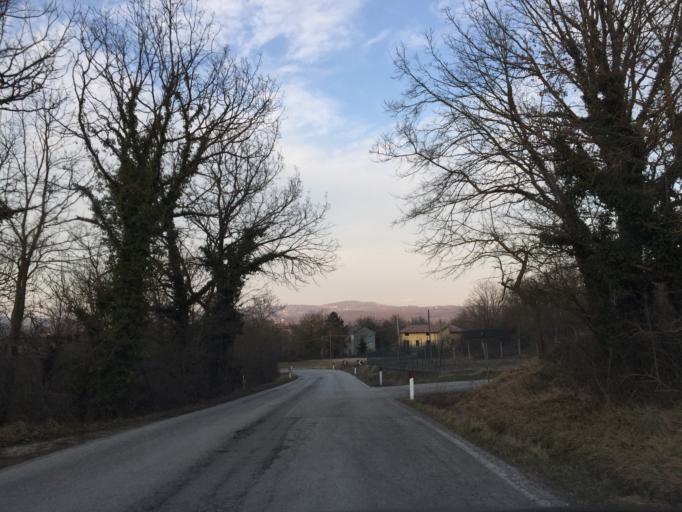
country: IT
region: Molise
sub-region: Provincia di Campobasso
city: Guardiaregia
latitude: 41.4511
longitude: 14.5553
